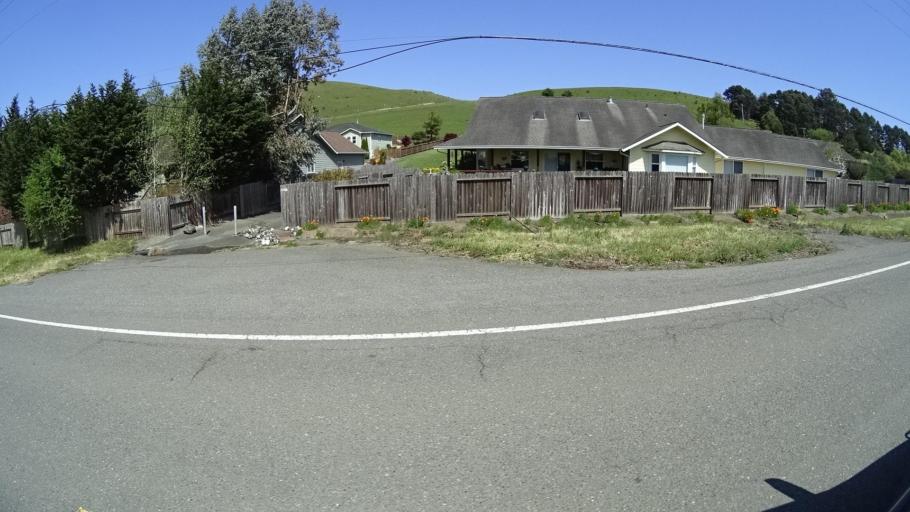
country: US
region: California
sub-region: Humboldt County
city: Hydesville
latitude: 40.5565
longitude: -124.1224
